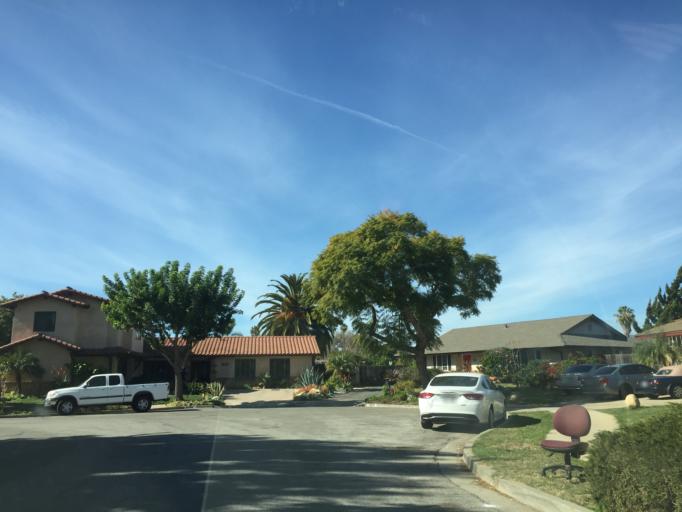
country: US
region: California
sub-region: Santa Barbara County
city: Goleta
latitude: 34.4361
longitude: -119.7853
